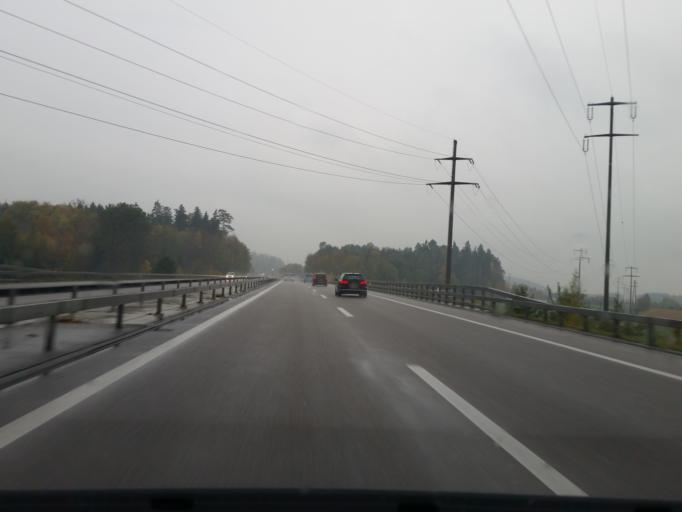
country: CH
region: Zurich
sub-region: Bezirk Winterthur
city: Sulz
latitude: 47.5397
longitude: 8.8111
